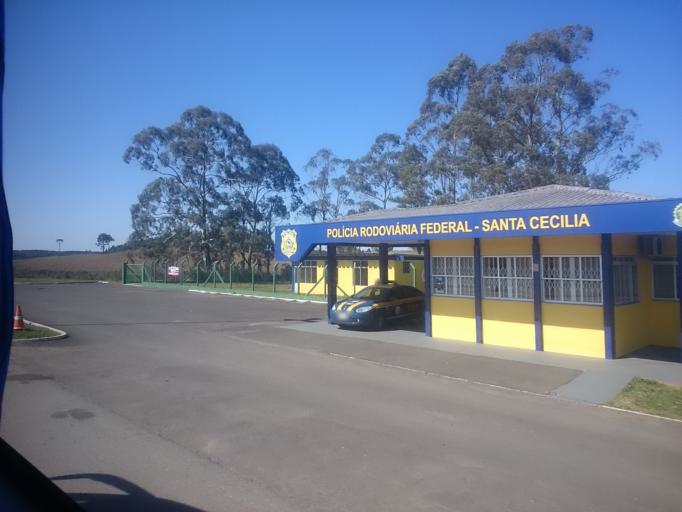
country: BR
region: Santa Catarina
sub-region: Santa Cecilia
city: Santa Cecilia
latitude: -26.8258
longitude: -50.3709
